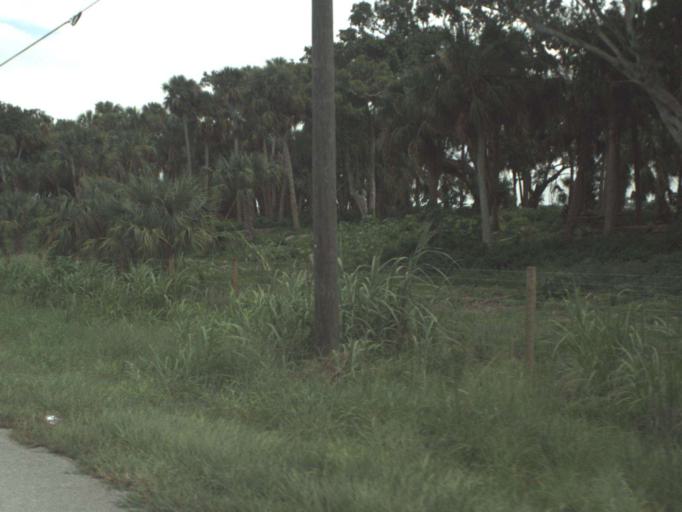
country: US
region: Florida
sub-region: Martin County
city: Indiantown
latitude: 27.0758
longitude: -80.6553
